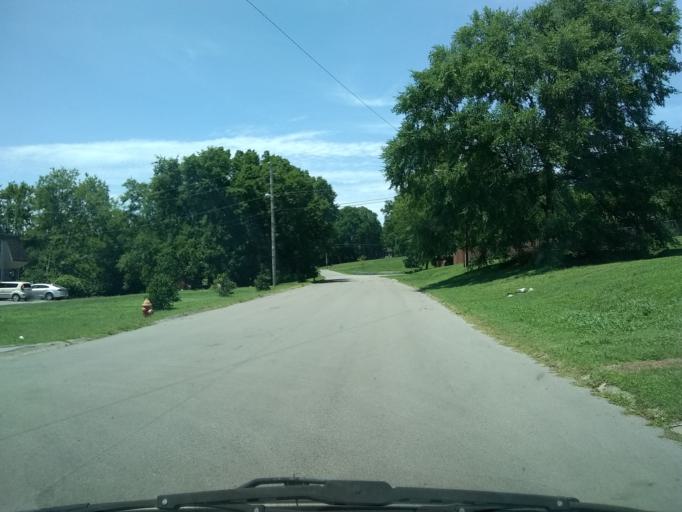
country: US
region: Tennessee
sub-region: Davidson County
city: Nashville
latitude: 36.1338
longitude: -86.7094
